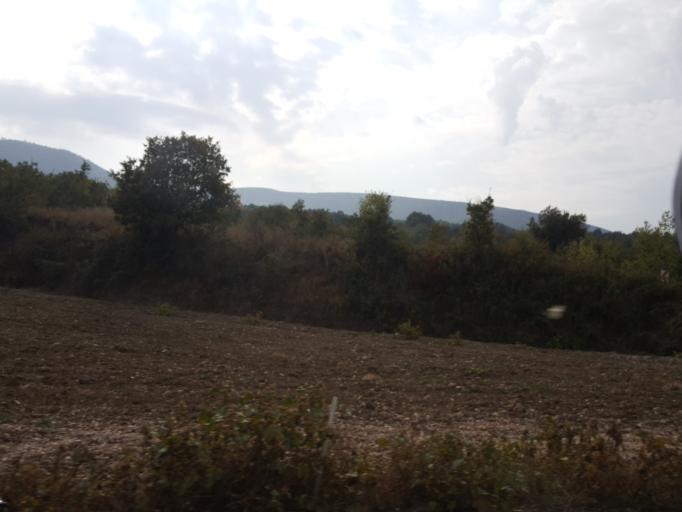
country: TR
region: Amasya
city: Gediksaray
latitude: 40.4847
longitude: 35.7796
